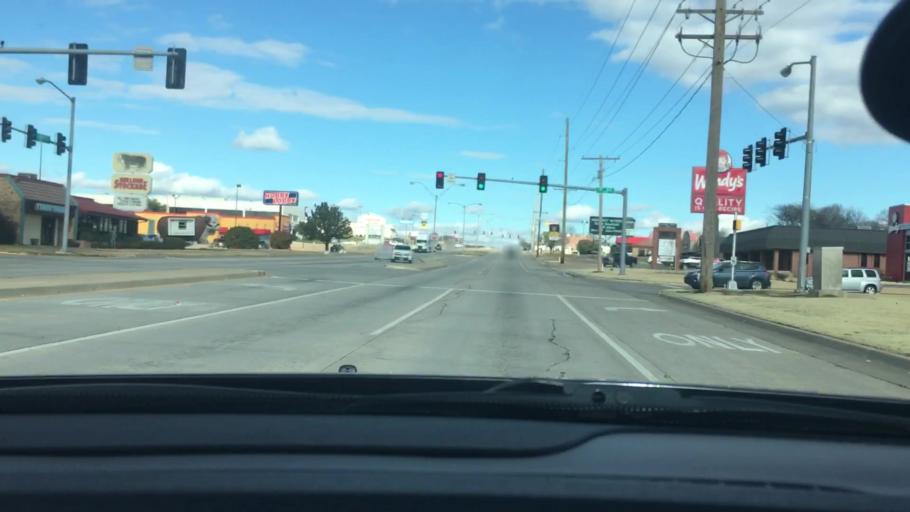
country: US
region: Oklahoma
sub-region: Carter County
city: Ardmore
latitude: 34.1894
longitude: -97.1430
